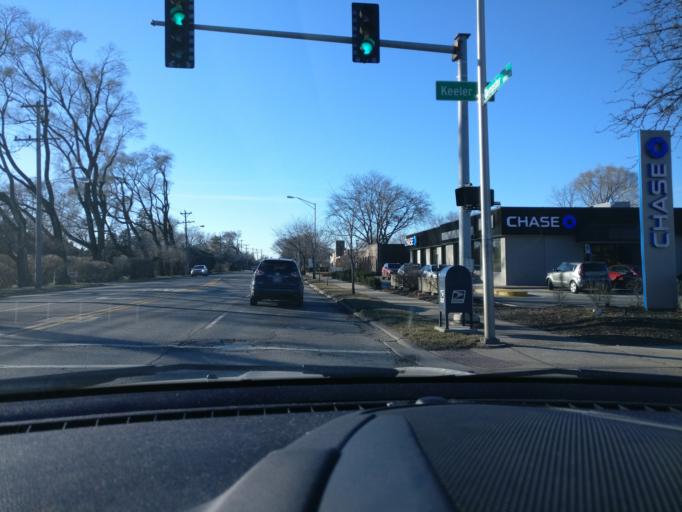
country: US
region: Illinois
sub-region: Cook County
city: Skokie
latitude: 42.0408
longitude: -87.7326
